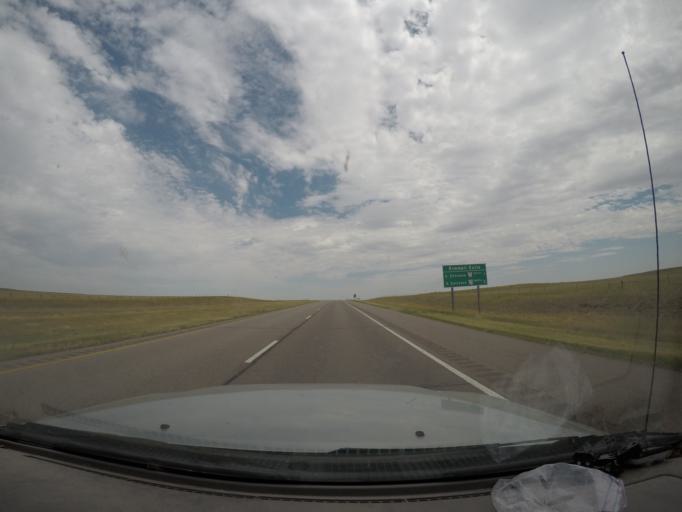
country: US
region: Nebraska
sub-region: Kimball County
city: Kimball
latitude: 41.2116
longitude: -103.6965
